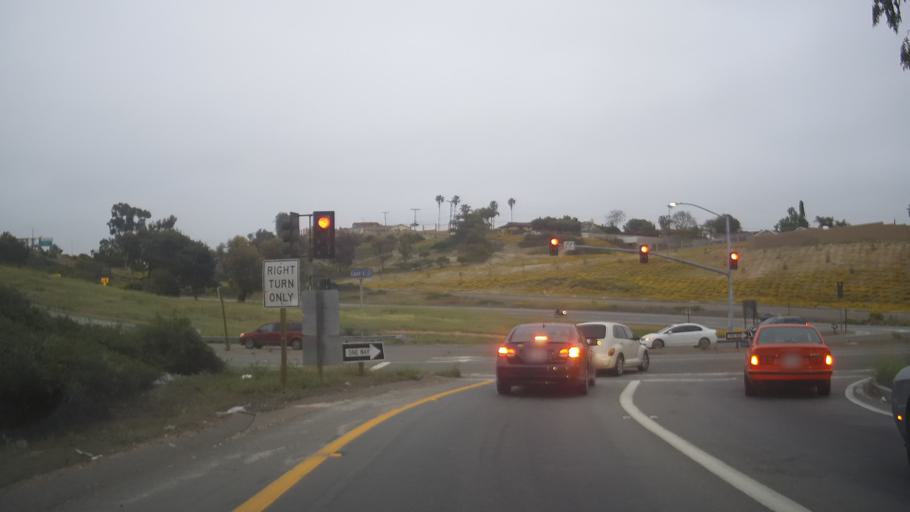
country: US
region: California
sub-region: San Diego County
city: Bonita
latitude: 32.6298
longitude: -117.0462
